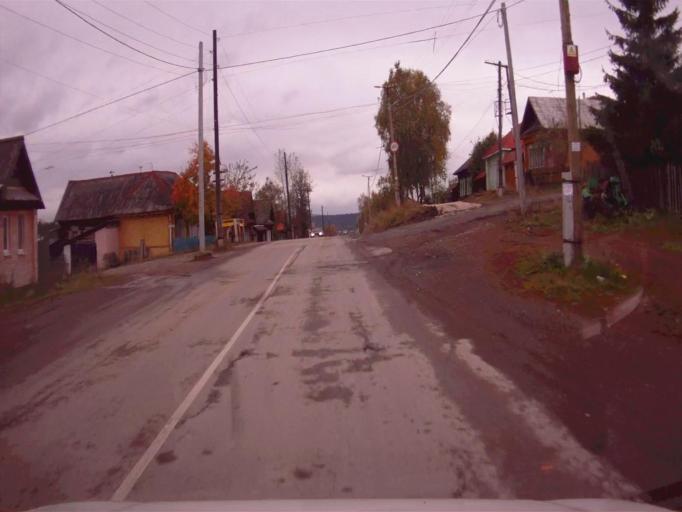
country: RU
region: Chelyabinsk
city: Nyazepetrovsk
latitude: 56.0602
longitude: 59.6119
